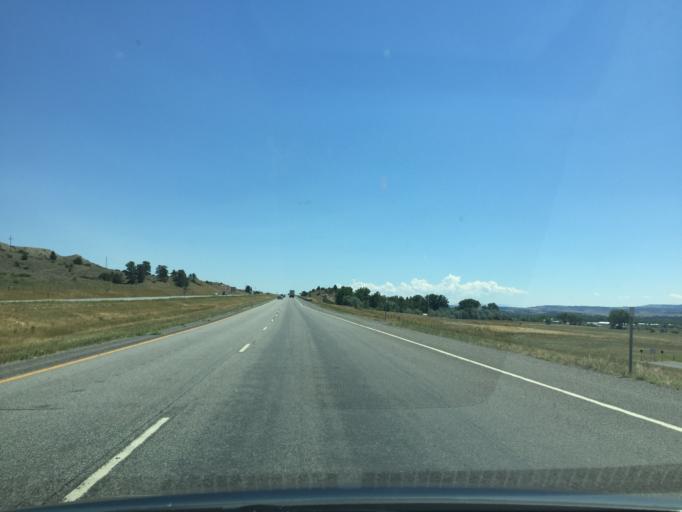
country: US
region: Montana
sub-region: Stillwater County
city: Columbus
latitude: 45.6443
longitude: -109.2423
